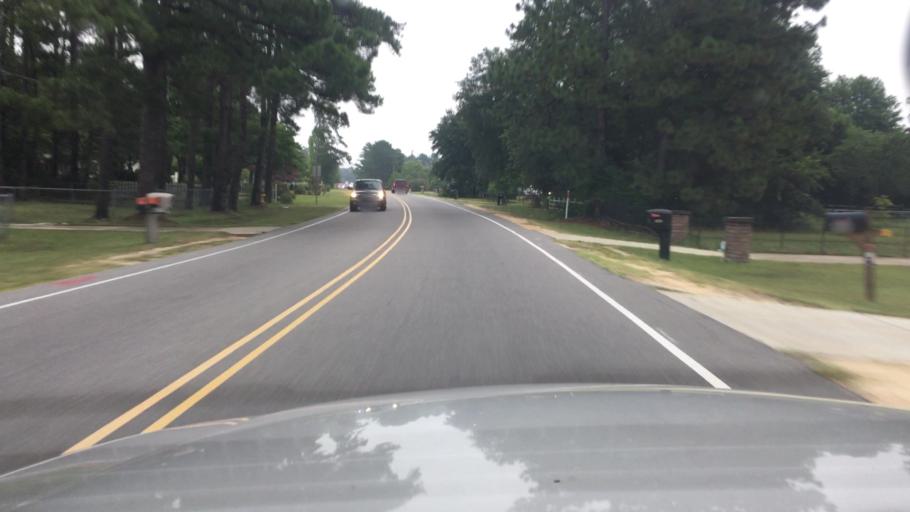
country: US
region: North Carolina
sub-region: Cumberland County
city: Hope Mills
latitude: 34.9755
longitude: -78.9950
